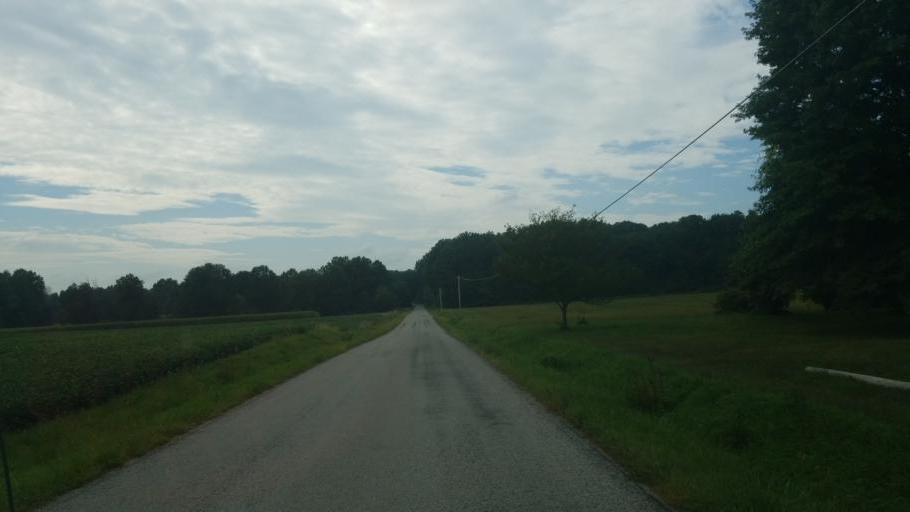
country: US
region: Ohio
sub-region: Wayne County
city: Creston
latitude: 40.9082
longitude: -81.9472
